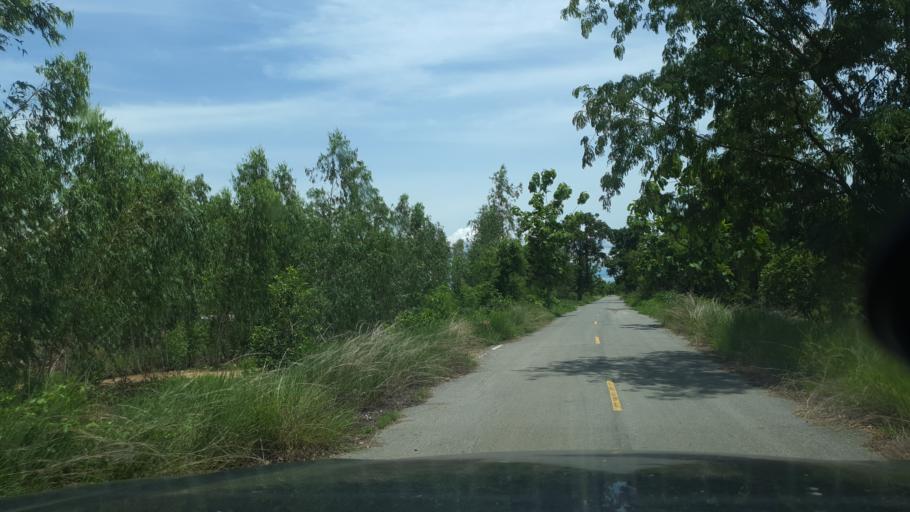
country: TH
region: Sukhothai
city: Ban Na
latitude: 17.1209
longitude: 99.6750
